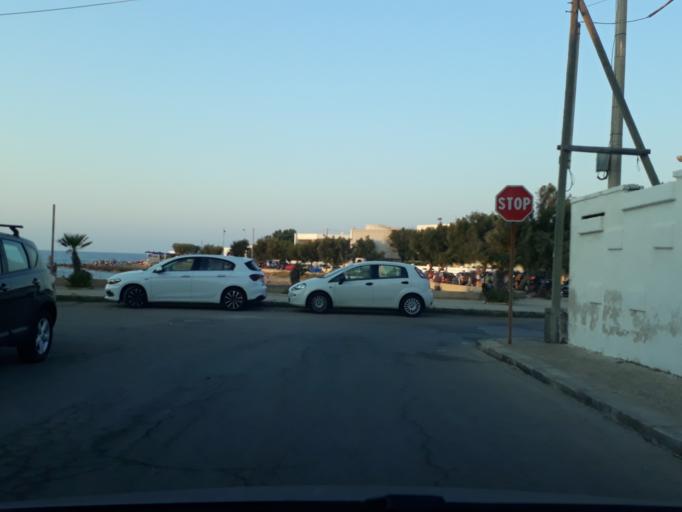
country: IT
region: Apulia
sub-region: Provincia di Brindisi
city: Carovigno
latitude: 40.7582
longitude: 17.7004
